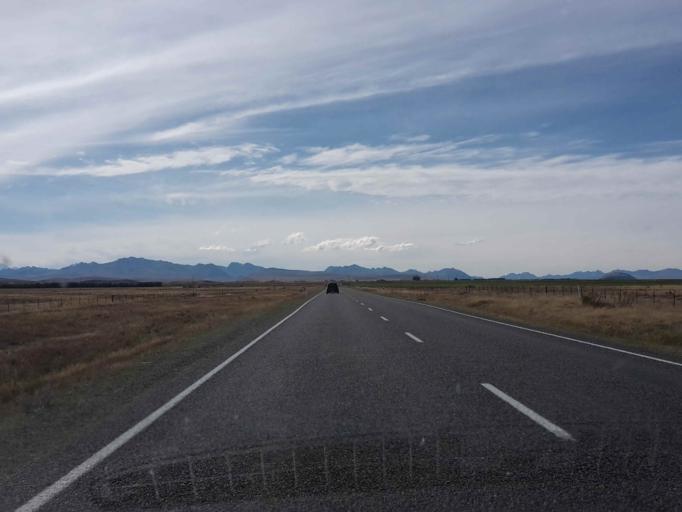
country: NZ
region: Canterbury
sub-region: Timaru District
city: Pleasant Point
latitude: -44.1664
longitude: 170.3335
